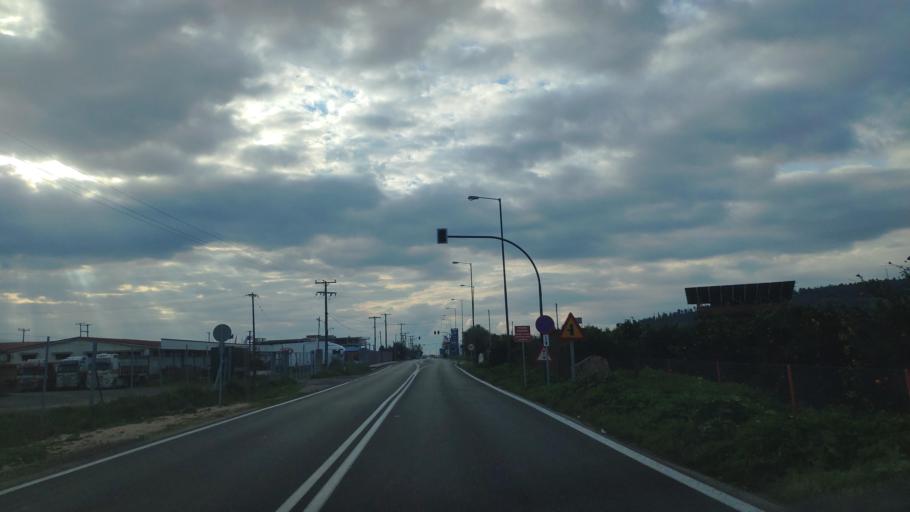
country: GR
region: Peloponnese
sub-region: Nomos Argolidos
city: Argos
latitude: 37.6538
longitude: 22.7276
